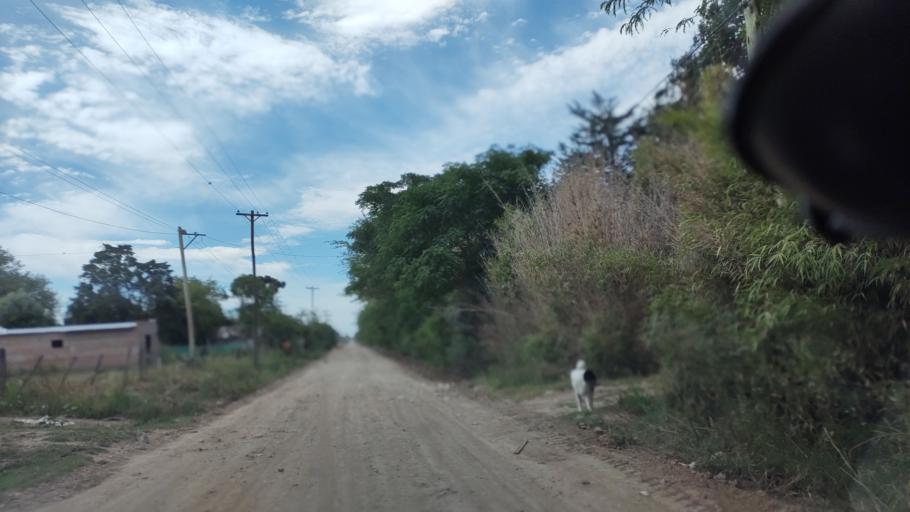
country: AR
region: Buenos Aires
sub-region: Partido de Lobos
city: Lobos
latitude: -35.1689
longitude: -59.1087
